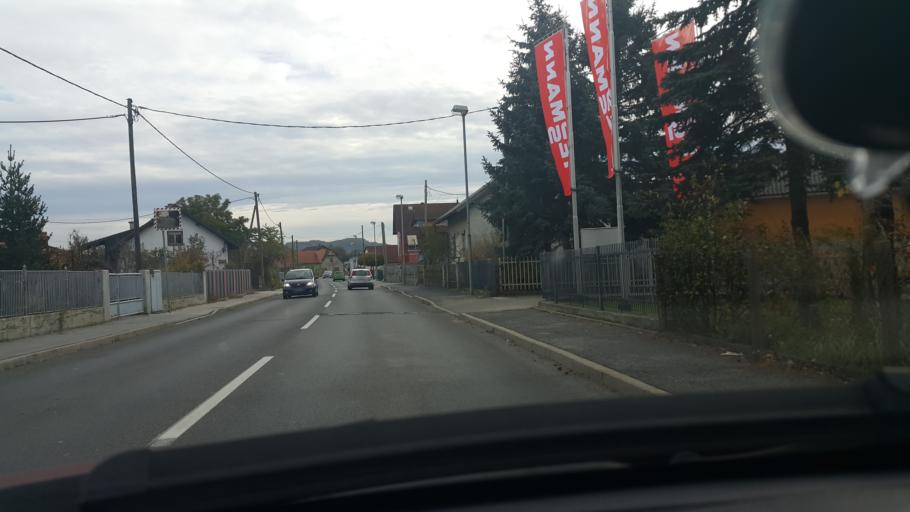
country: SI
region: Maribor
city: Maribor
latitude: 46.5440
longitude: 15.6786
